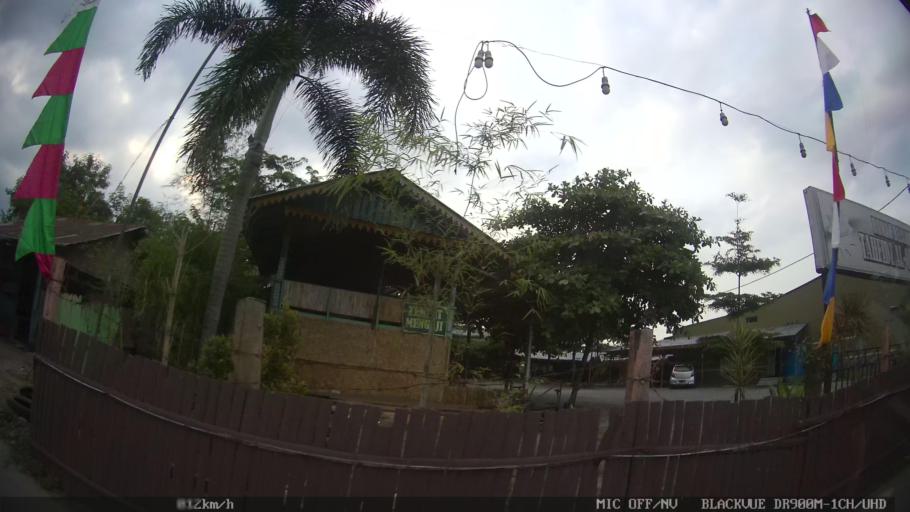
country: ID
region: North Sumatra
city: Sunggal
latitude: 3.5661
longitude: 98.6095
